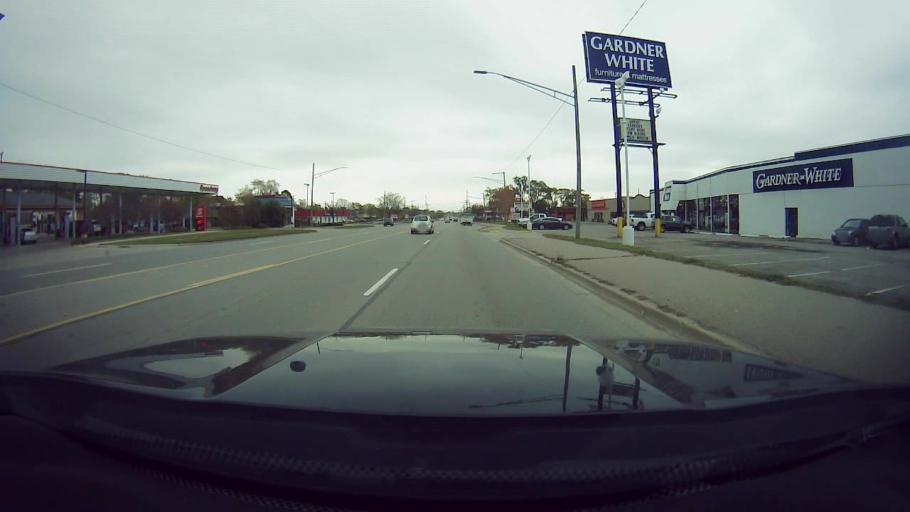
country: US
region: Michigan
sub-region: Oakland County
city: Waterford
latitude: 42.6915
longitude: -83.3880
